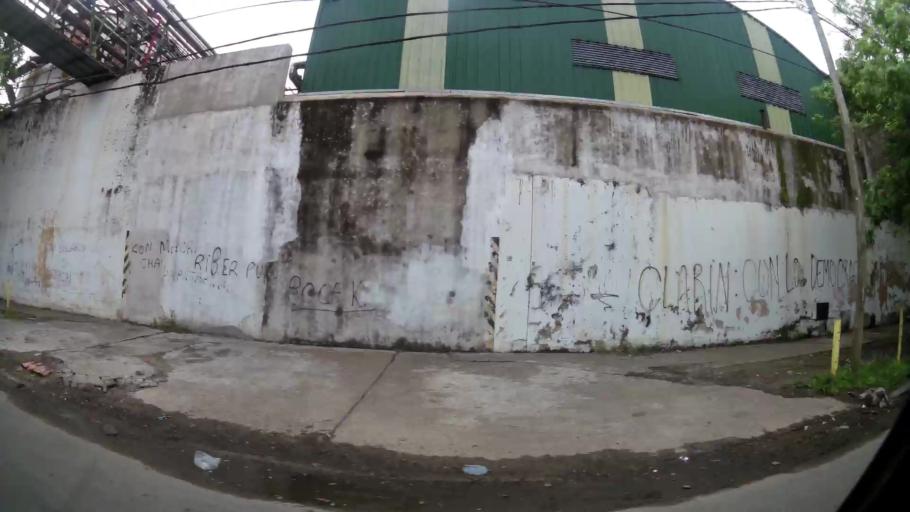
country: AR
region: Buenos Aires
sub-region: Partido de Lanus
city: Lanus
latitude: -34.7145
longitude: -58.3589
